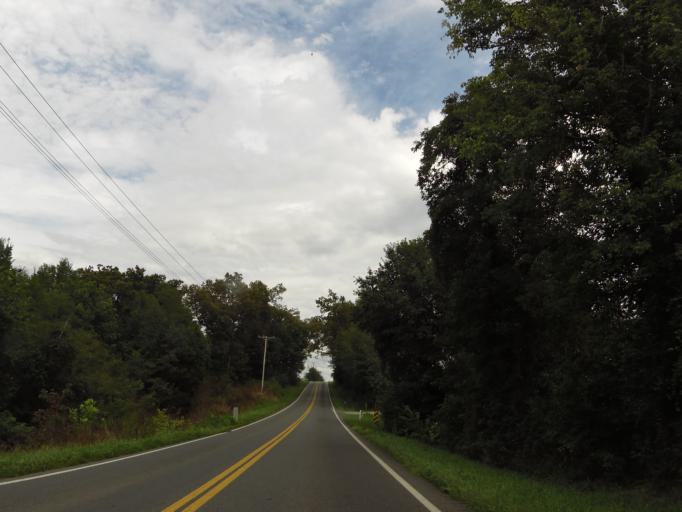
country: US
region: Kentucky
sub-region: McCracken County
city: Massac
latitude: 37.0206
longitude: -88.7847
